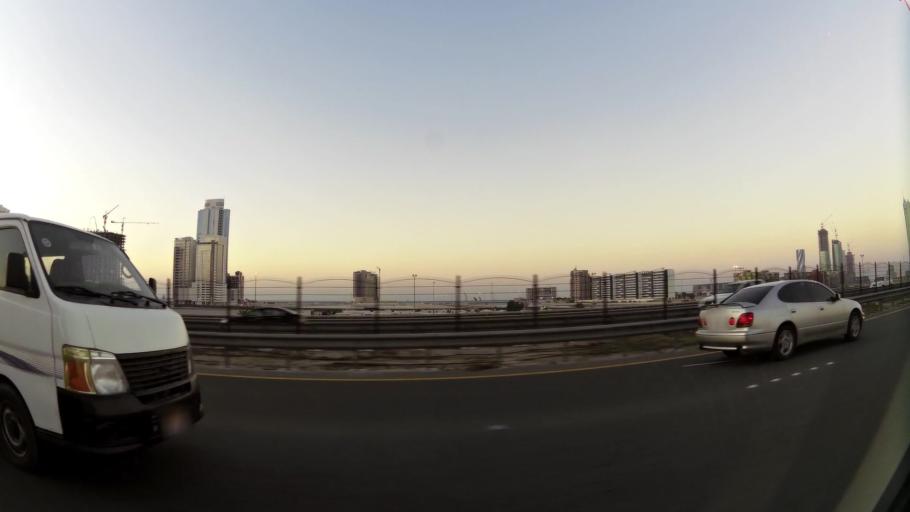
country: BH
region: Manama
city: Jidd Hafs
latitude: 26.2317
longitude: 50.5600
